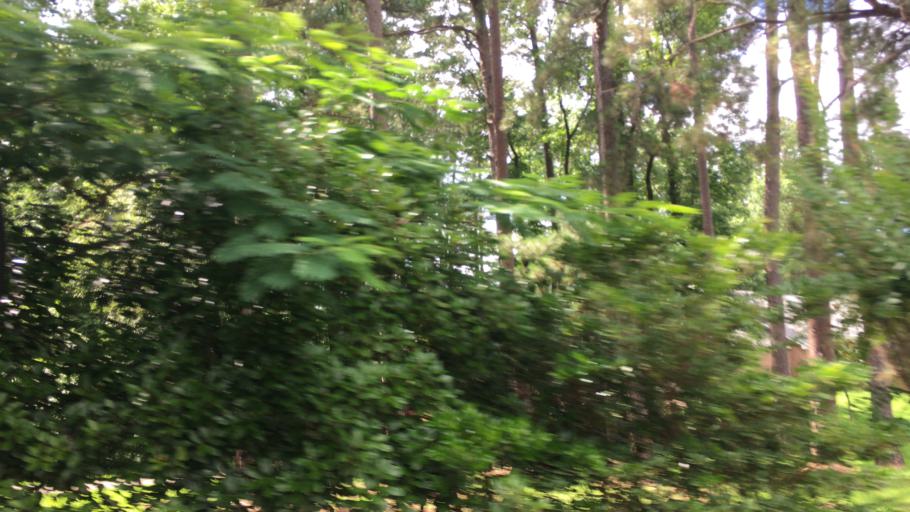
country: US
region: Louisiana
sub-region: Lincoln Parish
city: Ruston
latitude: 32.5490
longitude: -92.6322
